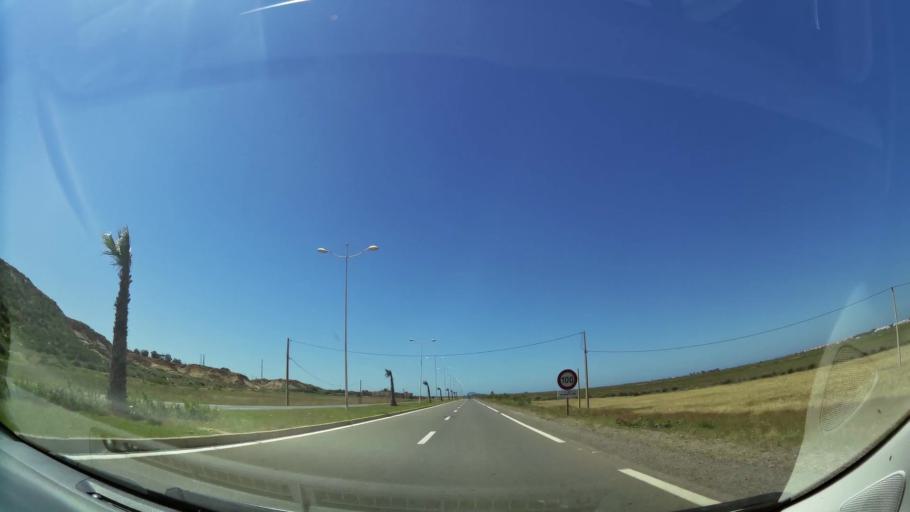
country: MA
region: Oriental
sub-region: Berkane-Taourirt
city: Madagh
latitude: 35.0970
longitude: -2.3177
